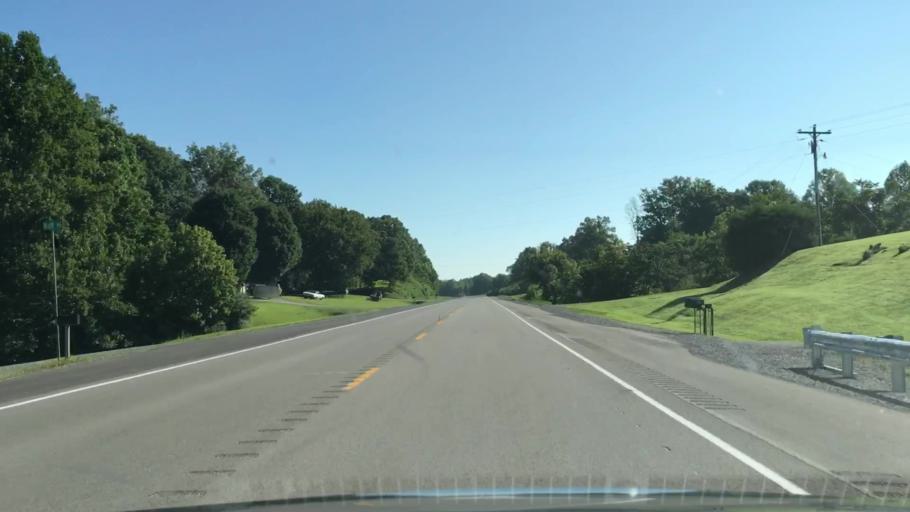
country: US
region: Tennessee
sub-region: Clay County
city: Celina
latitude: 36.6229
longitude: -85.4078
